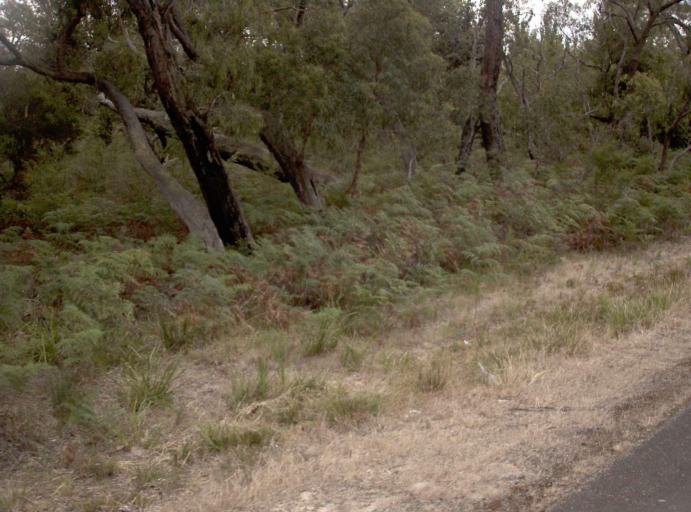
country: AU
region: Victoria
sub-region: Wellington
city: Sale
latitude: -38.2649
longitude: 147.0358
